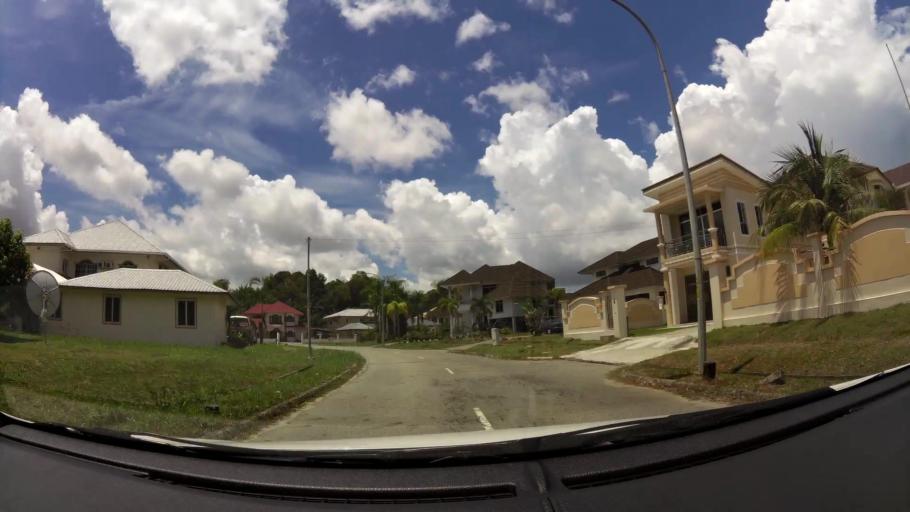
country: BN
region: Brunei and Muara
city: Bandar Seri Begawan
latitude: 4.9637
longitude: 114.9108
